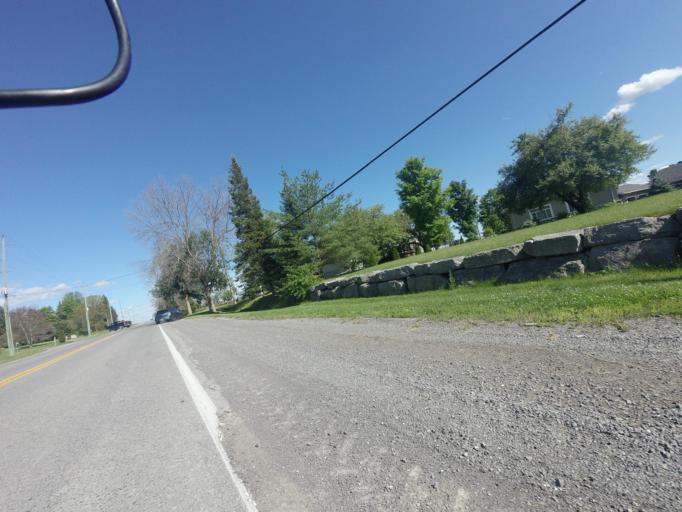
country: CA
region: Ontario
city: Arnprior
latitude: 45.4171
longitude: -76.4243
